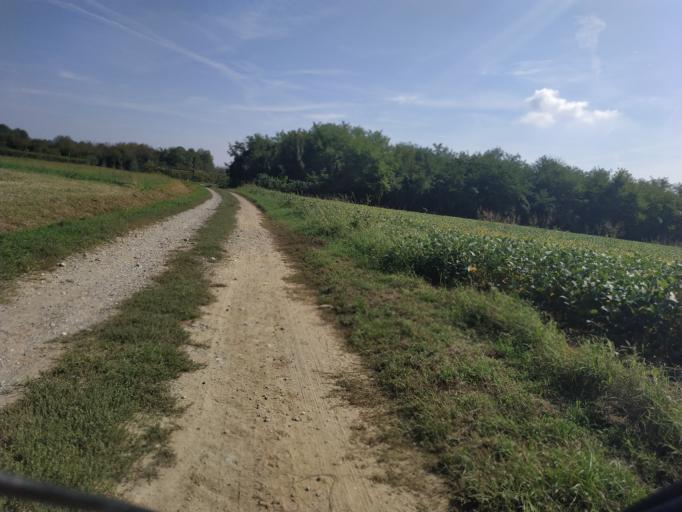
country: IT
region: Piedmont
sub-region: Provincia di Torino
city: Orio Canavese
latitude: 45.3220
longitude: 7.8536
